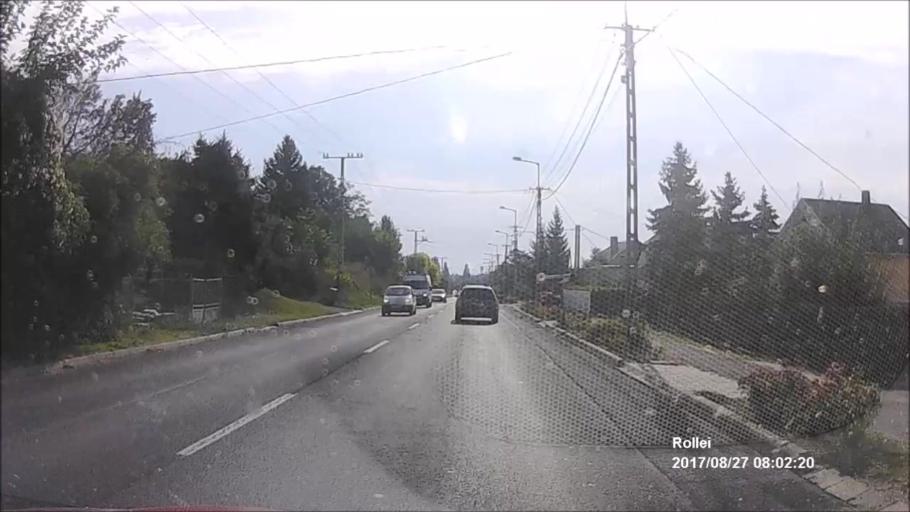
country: HU
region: Zala
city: Vonyarcvashegy
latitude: 46.7611
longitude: 17.3204
